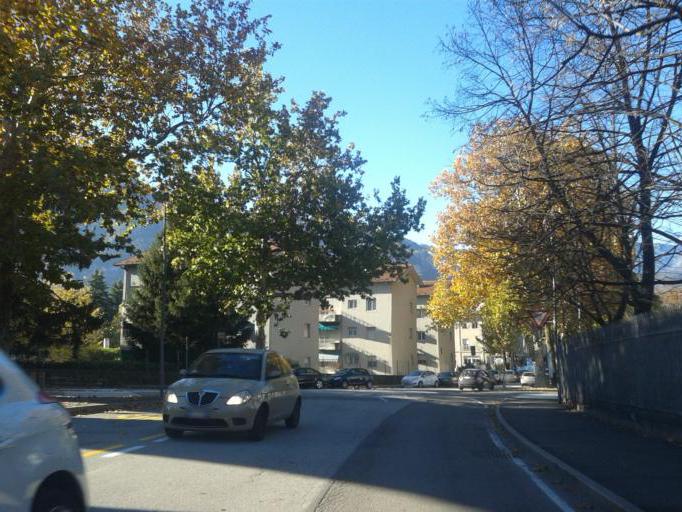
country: IT
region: Trentino-Alto Adige
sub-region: Provincia di Trento
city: Trento
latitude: 46.0550
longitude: 11.1336
